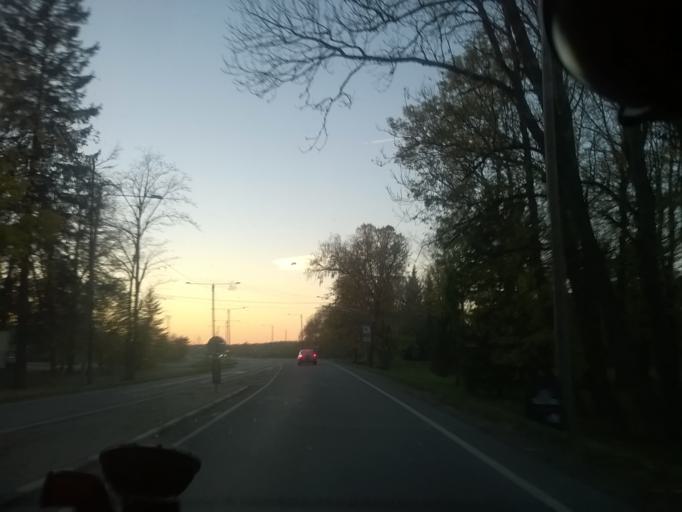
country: EE
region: Laeaene
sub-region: Ridala Parish
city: Uuemoisa
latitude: 58.9568
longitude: 23.7452
